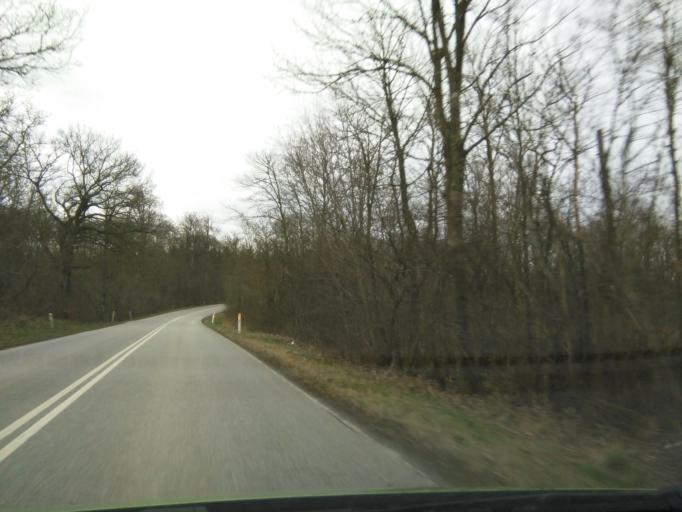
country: DK
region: North Denmark
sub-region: Mariagerfjord Kommune
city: Mariager
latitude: 56.5985
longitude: 9.9987
